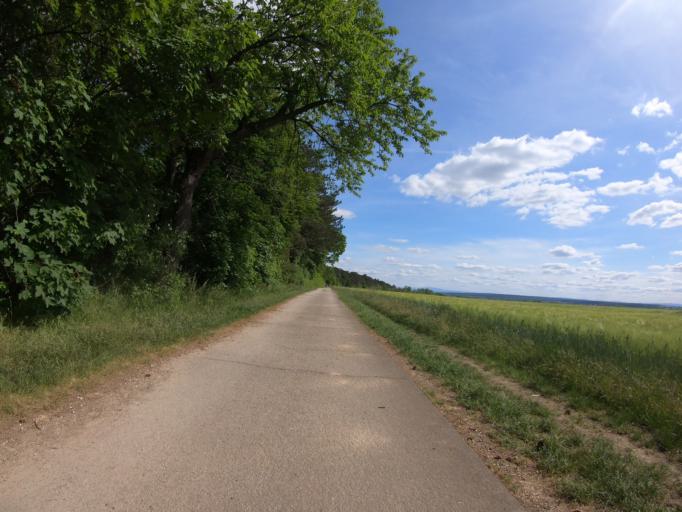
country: DE
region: Lower Saxony
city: Leiferde
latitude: 52.1910
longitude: 10.5266
